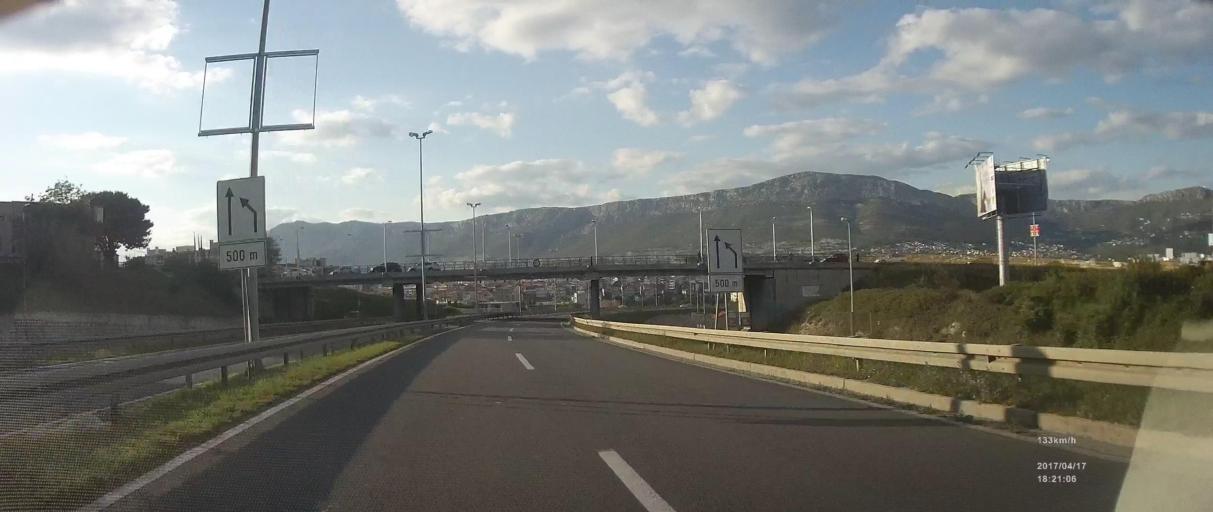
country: HR
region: Splitsko-Dalmatinska
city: Vranjic
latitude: 43.5152
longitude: 16.4819
